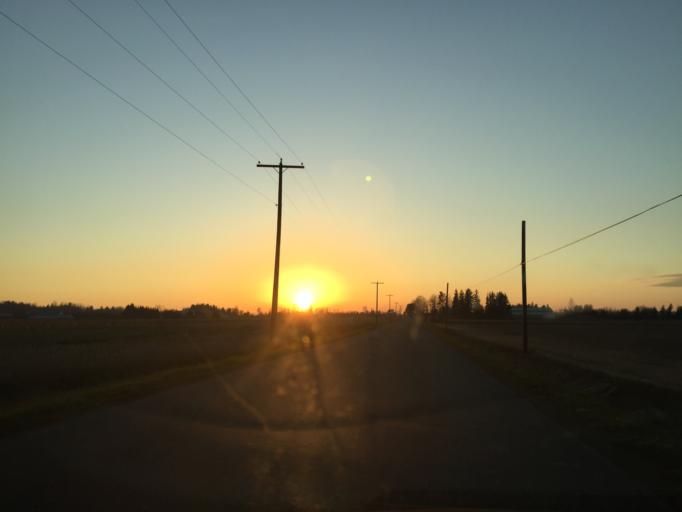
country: US
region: Washington
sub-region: Whatcom County
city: Sumas
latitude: 48.9816
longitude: -122.2240
